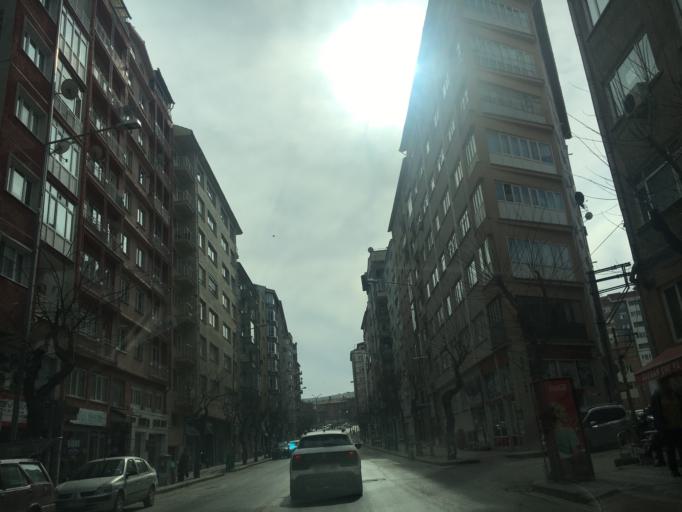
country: TR
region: Eskisehir
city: Eskisehir
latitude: 39.7672
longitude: 30.5192
